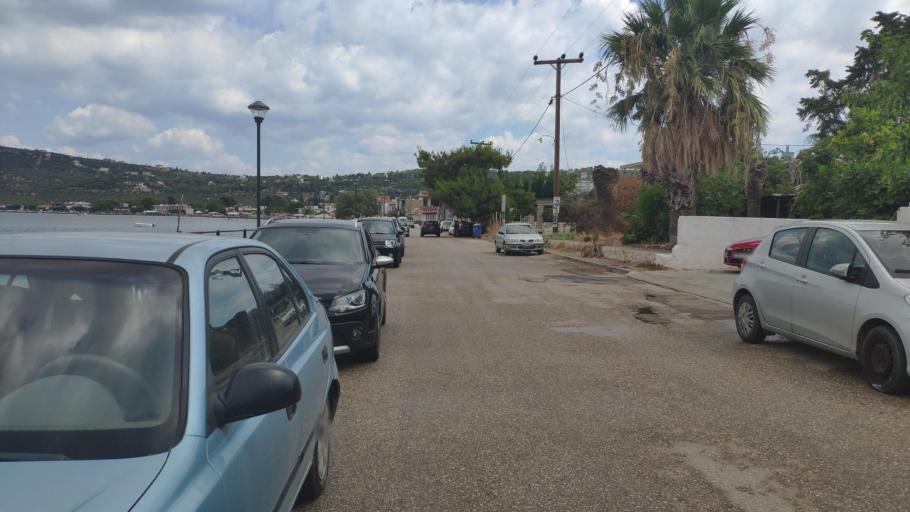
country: GR
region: Central Greece
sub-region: Nomos Fthiotidos
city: Malesina
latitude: 38.6505
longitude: 23.1908
